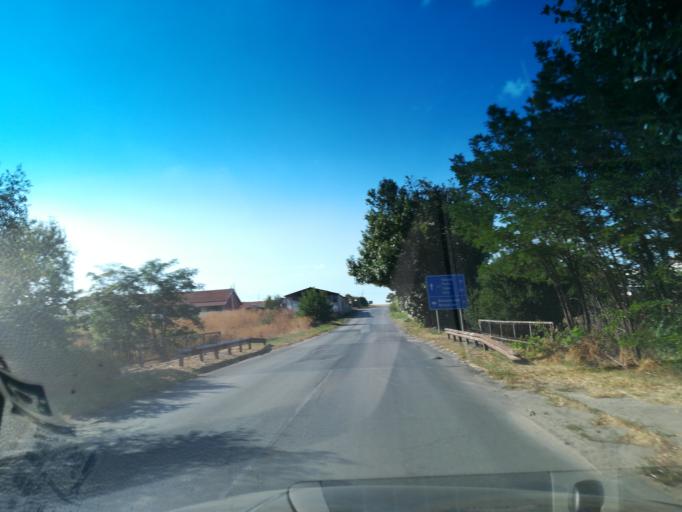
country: BG
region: Khaskovo
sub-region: Obshtina Mineralni Bani
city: Mineralni Bani
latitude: 42.0199
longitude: 25.4150
